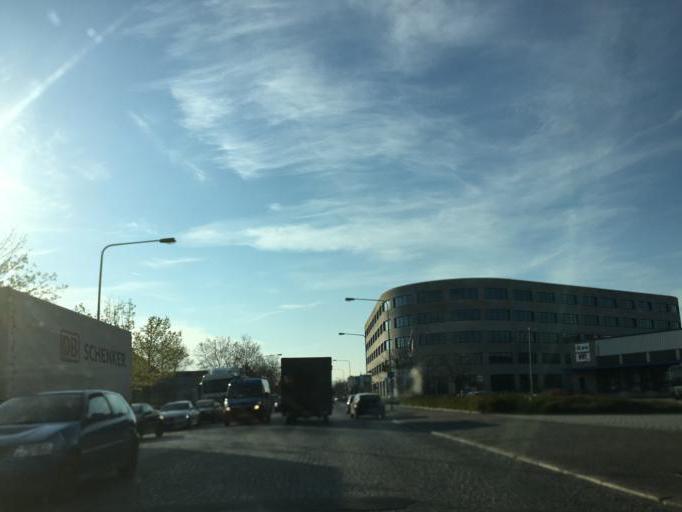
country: DE
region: Hesse
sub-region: Regierungsbezirk Darmstadt
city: Offenbach
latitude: 50.1206
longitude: 8.7527
